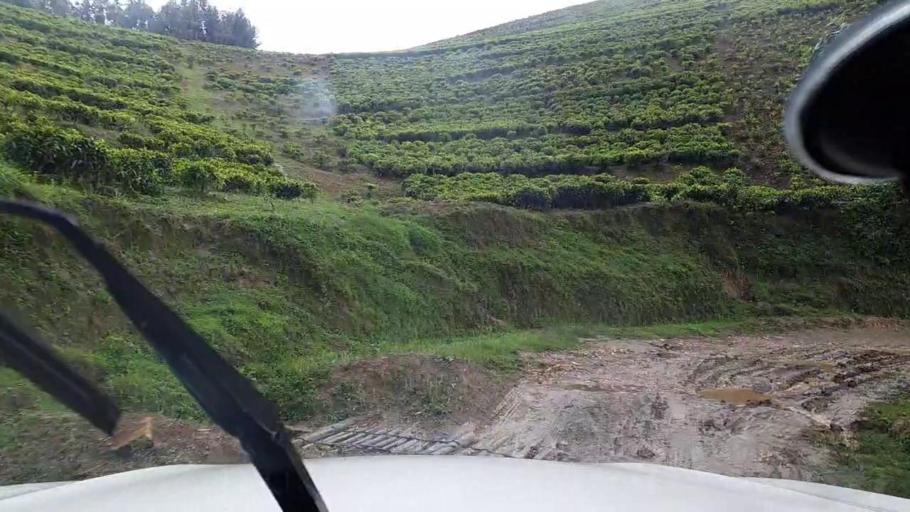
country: RW
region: Western Province
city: Kibuye
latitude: -2.0806
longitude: 29.5159
